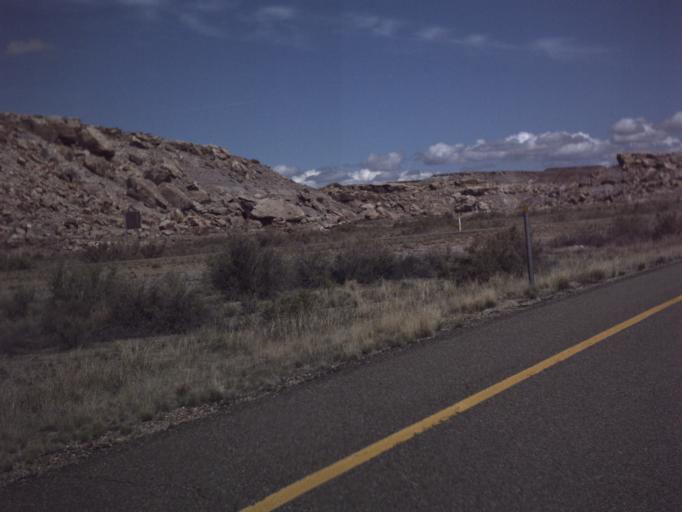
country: US
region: Utah
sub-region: Carbon County
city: East Carbon City
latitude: 38.9235
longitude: -110.3723
